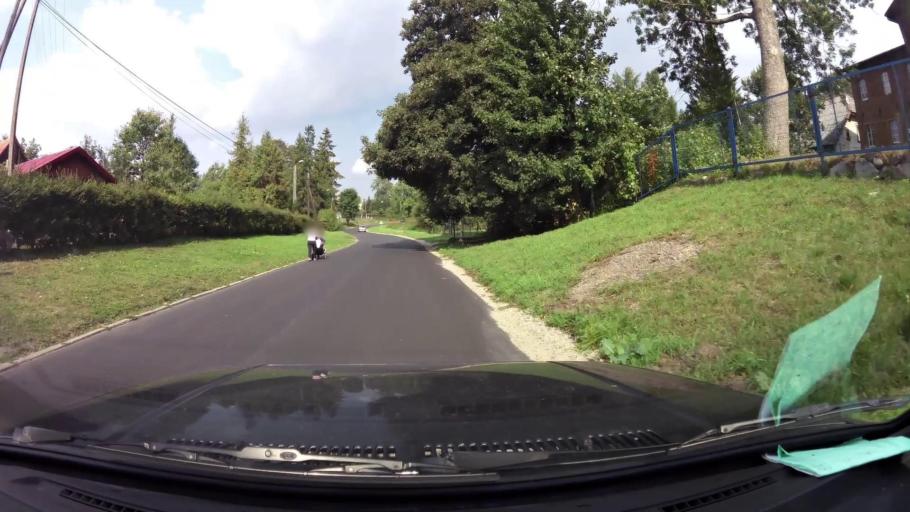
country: PL
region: Pomeranian Voivodeship
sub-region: Powiat slupski
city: Kepice
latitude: 54.1670
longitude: 16.8209
